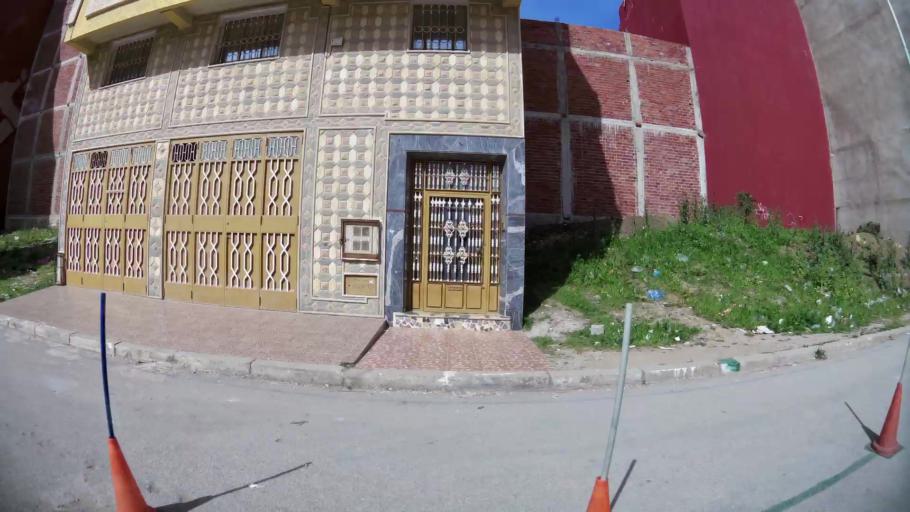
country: MA
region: Tanger-Tetouan
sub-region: Tanger-Assilah
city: Tangier
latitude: 35.7254
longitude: -5.8118
